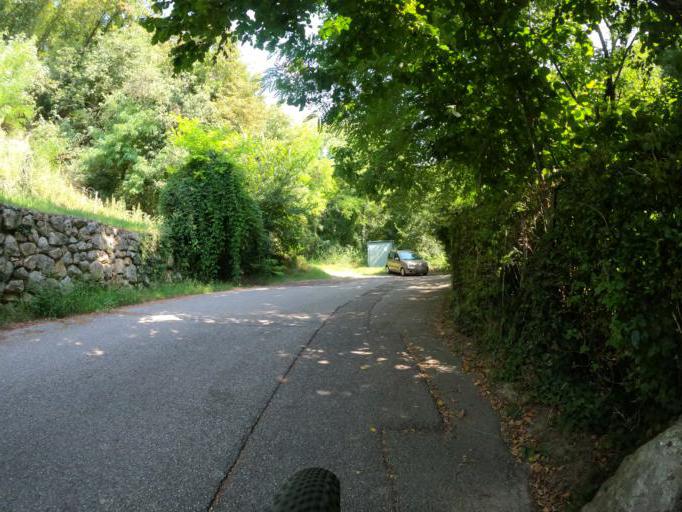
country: IT
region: Veneto
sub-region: Provincia di Verona
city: Caprino Veronese
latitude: 45.6238
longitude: 10.8181
